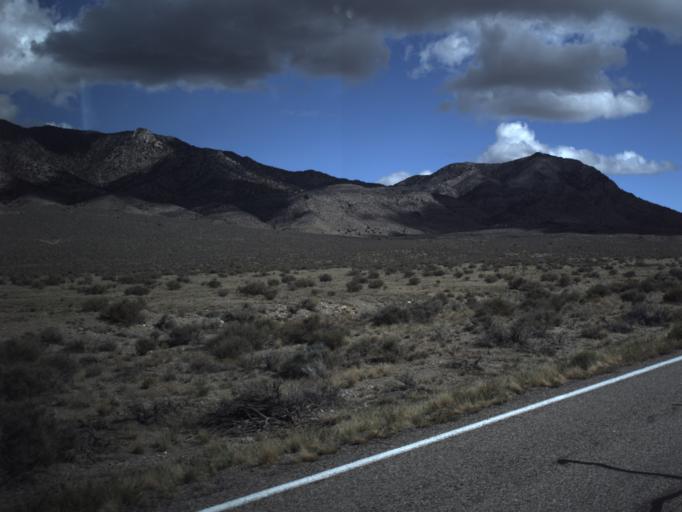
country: US
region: Utah
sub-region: Beaver County
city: Milford
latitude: 38.4450
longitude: -113.3289
